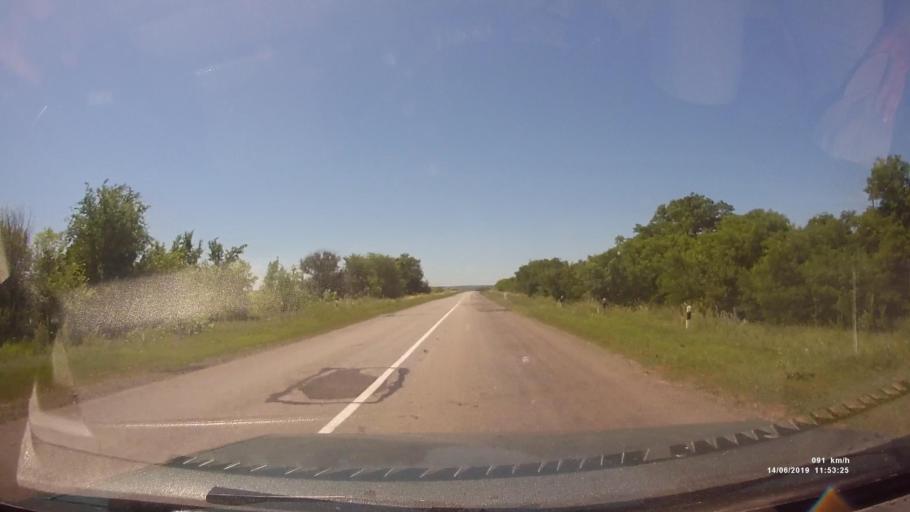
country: RU
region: Rostov
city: Kazanskaya
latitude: 49.8278
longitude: 41.2124
